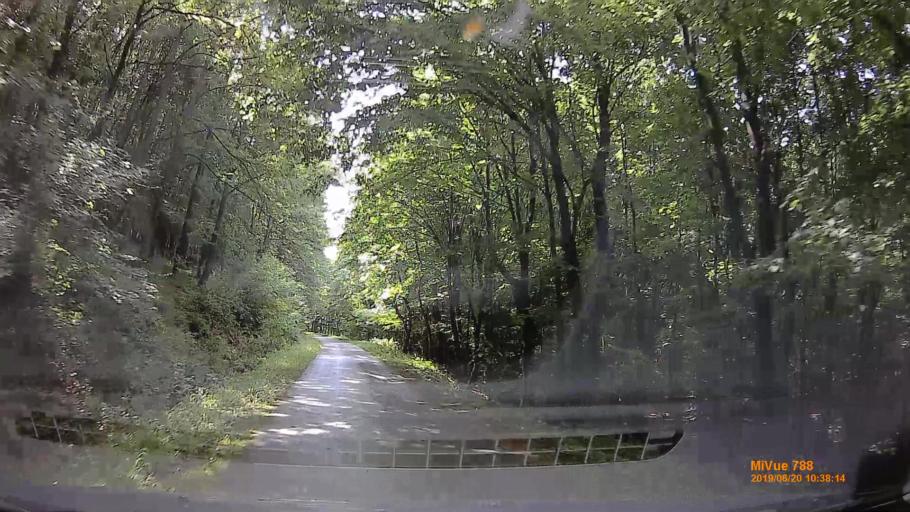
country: HU
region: Baranya
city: Hidas
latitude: 46.2010
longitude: 18.5362
